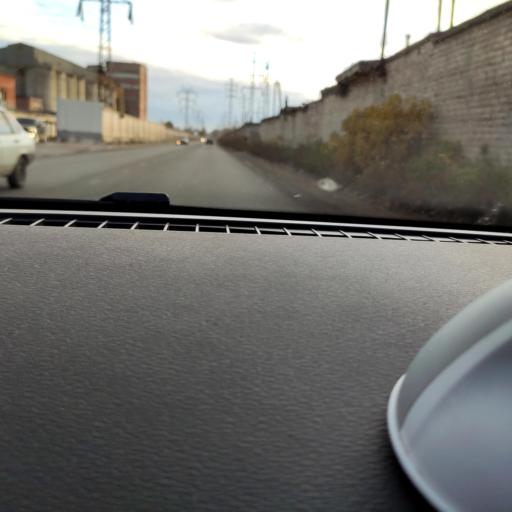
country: RU
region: Samara
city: Petra-Dubrava
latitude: 53.2494
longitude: 50.2940
